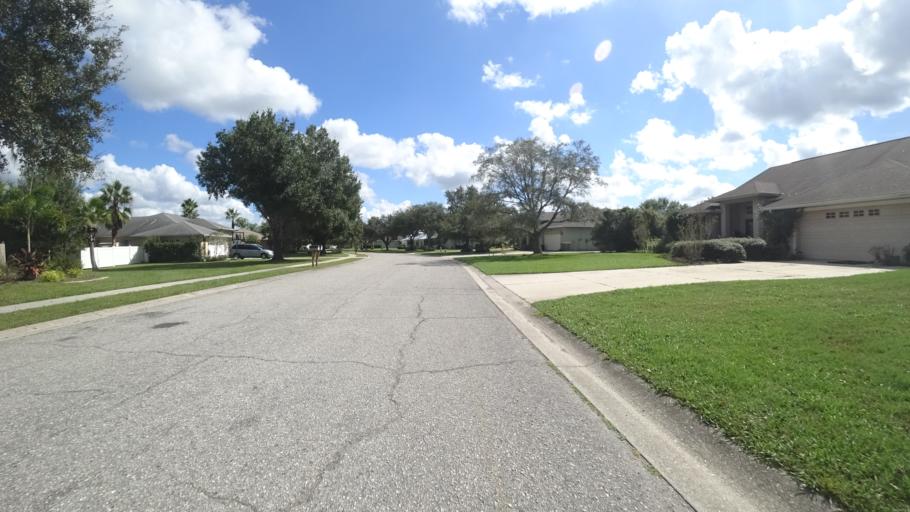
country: US
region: Florida
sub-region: Manatee County
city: Ellenton
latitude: 27.5020
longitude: -82.4047
